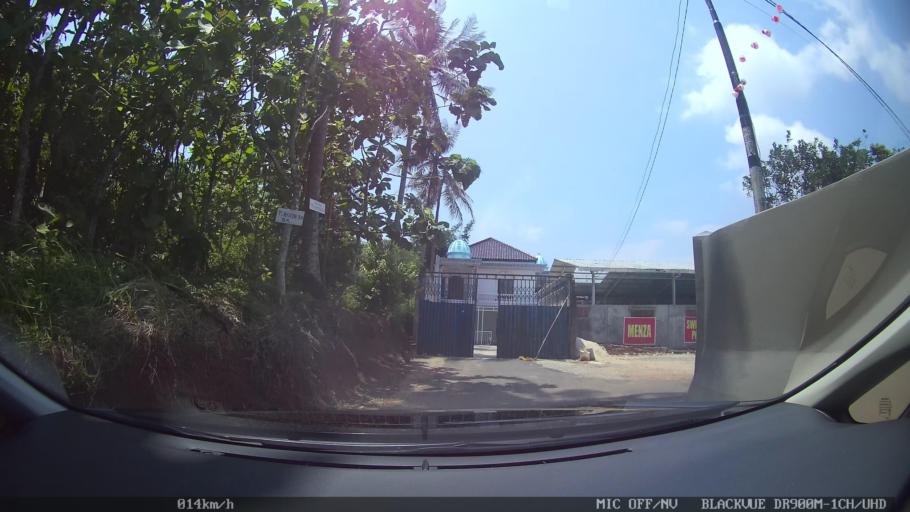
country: ID
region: Lampung
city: Kedaton
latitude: -5.3668
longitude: 105.2640
